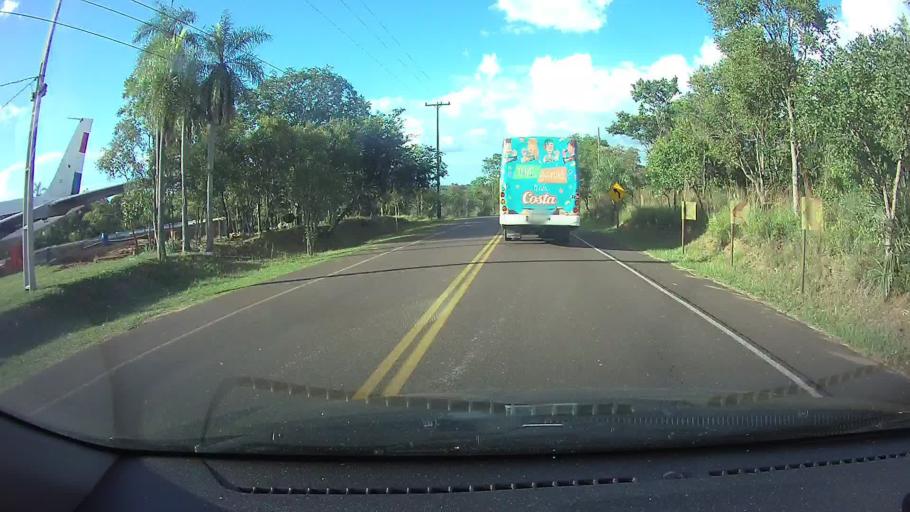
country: PY
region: Cordillera
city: Altos
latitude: -25.1998
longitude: -57.2230
